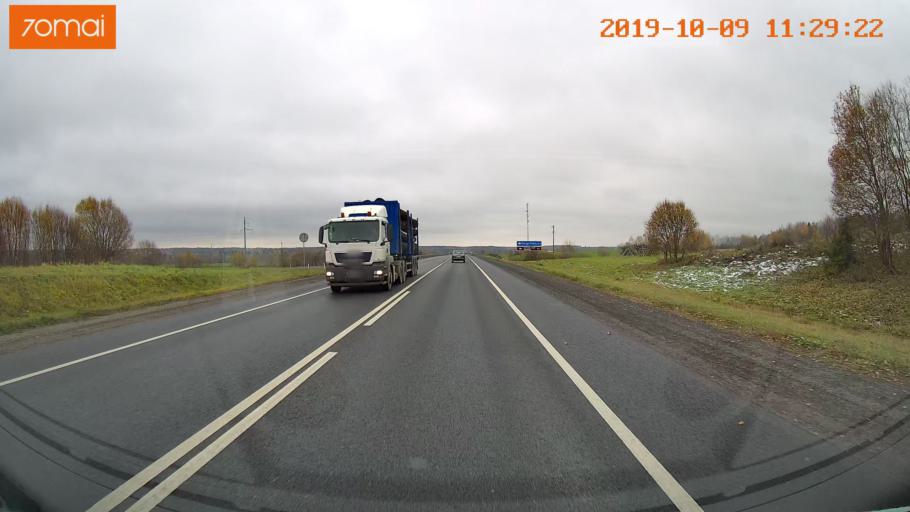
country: RU
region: Vologda
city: Vologda
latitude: 59.0631
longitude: 40.0514
